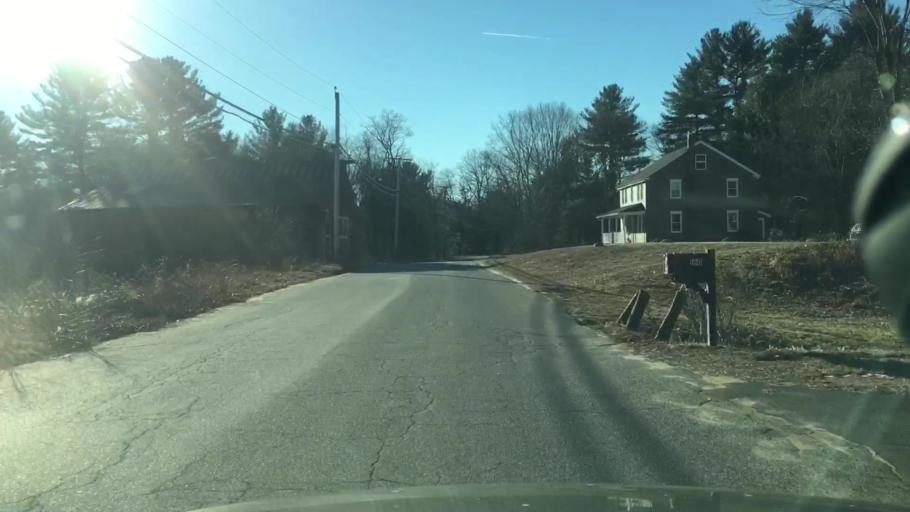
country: US
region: Connecticut
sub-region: Tolland County
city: Stafford
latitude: 41.9775
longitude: -72.2970
